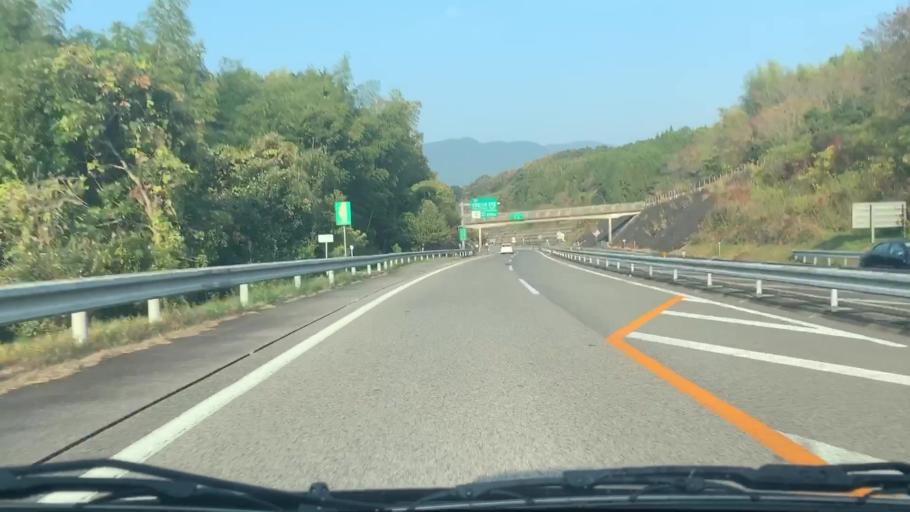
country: JP
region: Saga Prefecture
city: Imaricho-ko
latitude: 33.1670
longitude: 129.8566
